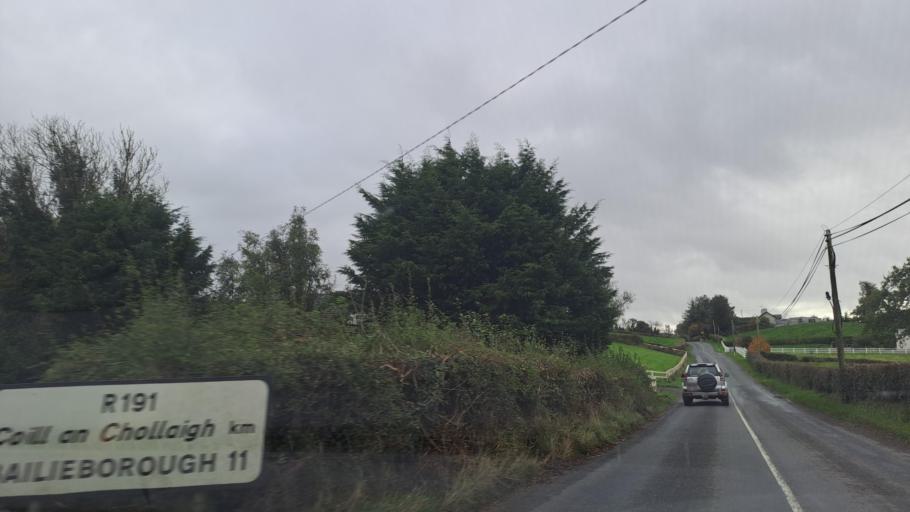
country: IE
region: Ulster
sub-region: An Cabhan
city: Bailieborough
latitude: 53.9767
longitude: -7.0457
